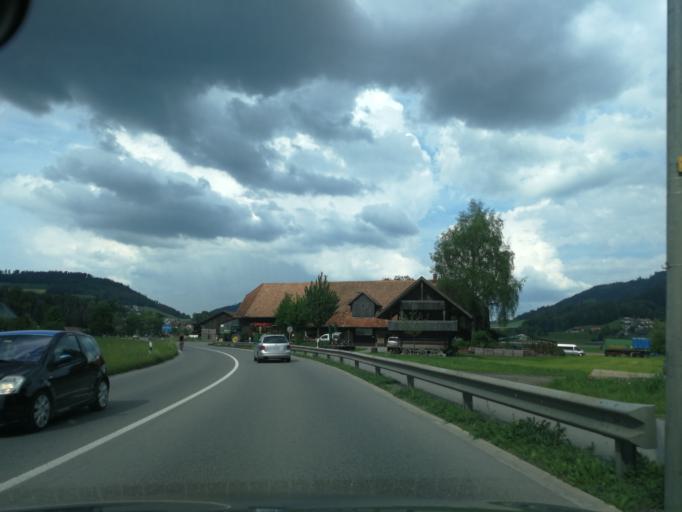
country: CH
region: Lucerne
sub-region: Entlebuch District
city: Oberdiessbach
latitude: 46.8217
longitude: 7.5999
